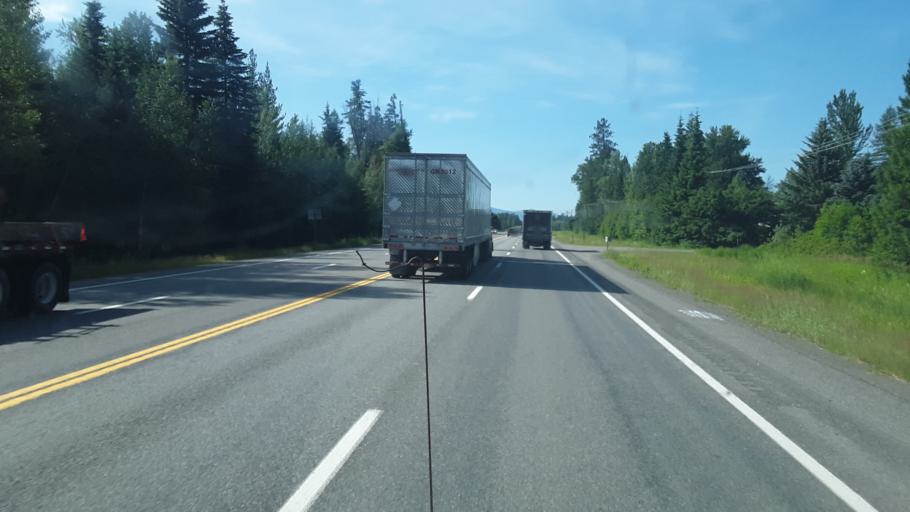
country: US
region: Idaho
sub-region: Bonner County
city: Ponderay
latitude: 48.3616
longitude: -116.5473
